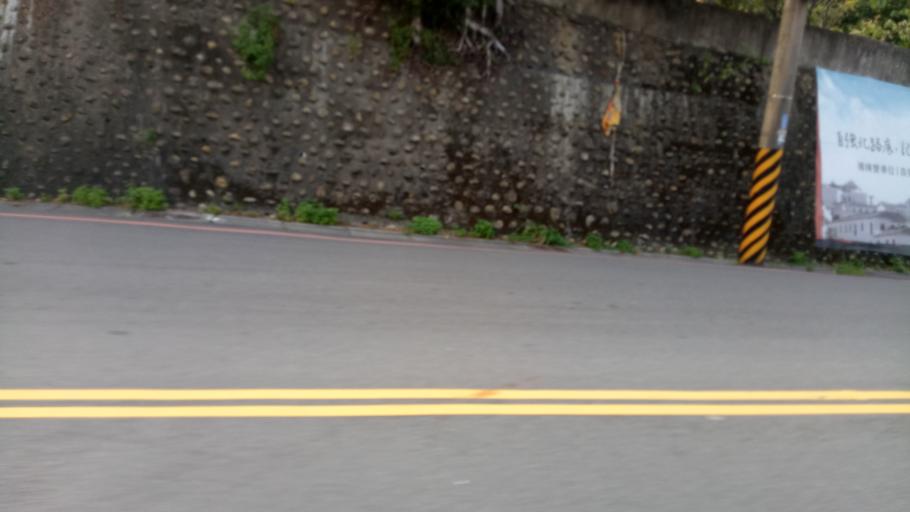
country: TW
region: Taiwan
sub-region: Hsinchu
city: Hsinchu
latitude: 24.7797
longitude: 120.9677
